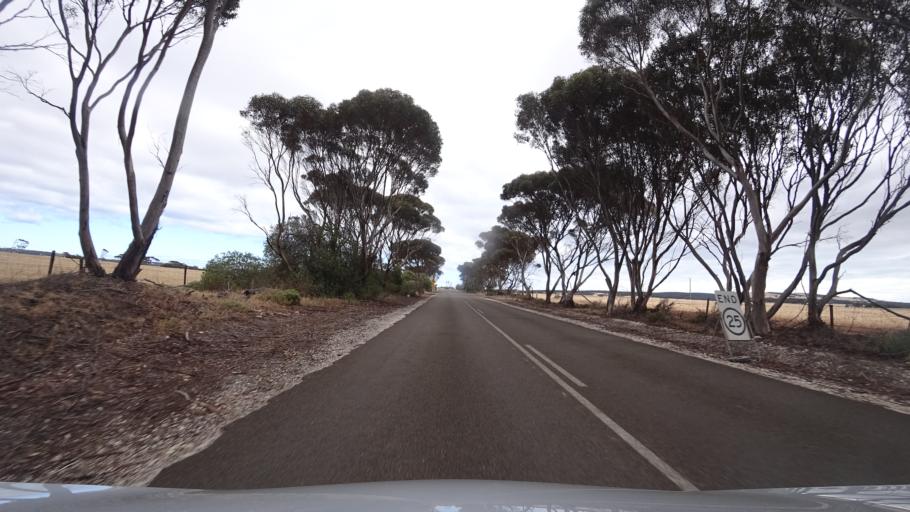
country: AU
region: South Australia
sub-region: Kangaroo Island
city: Kingscote
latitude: -35.6216
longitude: 137.5304
